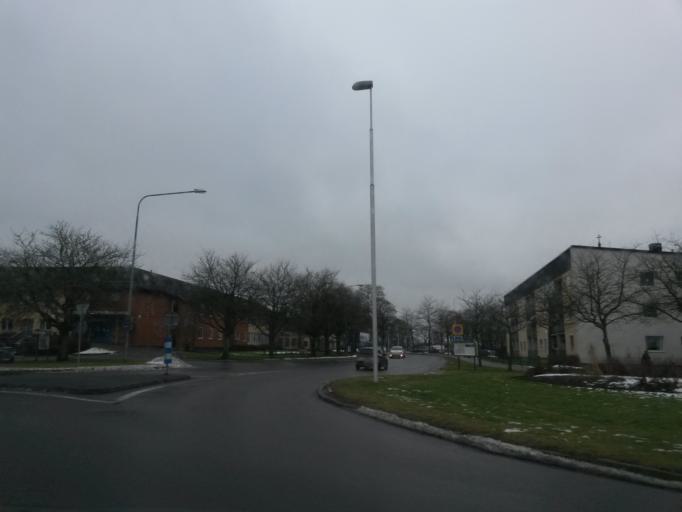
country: SE
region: Vaestra Goetaland
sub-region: Marks Kommun
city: Kinna
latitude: 57.5096
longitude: 12.6989
